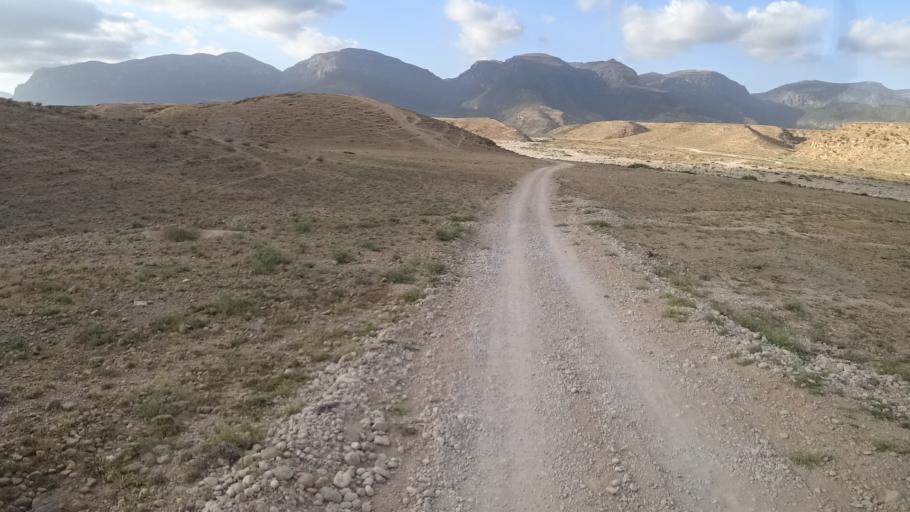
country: OM
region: Zufar
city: Salalah
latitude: 16.9752
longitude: 53.8528
